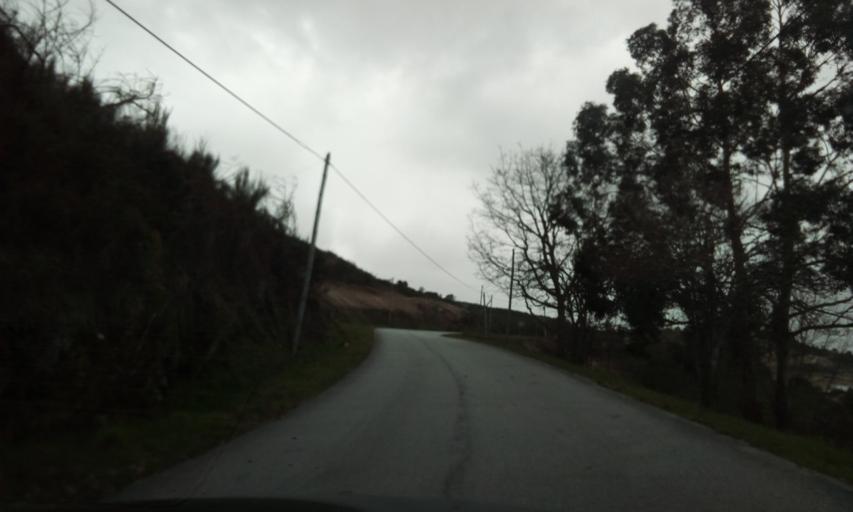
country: PT
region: Guarda
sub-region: Fornos de Algodres
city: Fornos de Algodres
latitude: 40.6366
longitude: -7.6055
